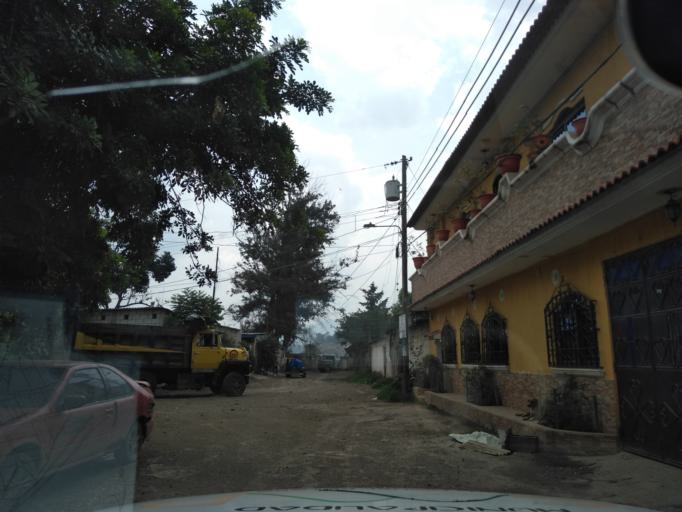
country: GT
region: Guatemala
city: Petapa
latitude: 14.5107
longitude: -90.5542
